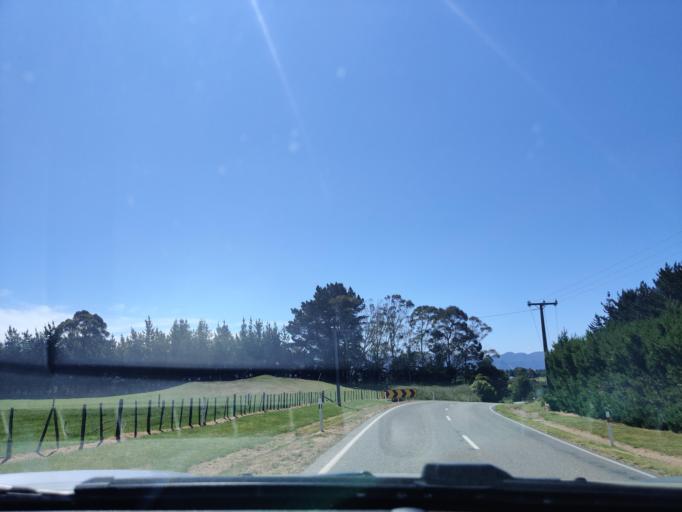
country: NZ
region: Wellington
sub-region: South Wairarapa District
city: Waipawa
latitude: -41.3023
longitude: 175.2711
